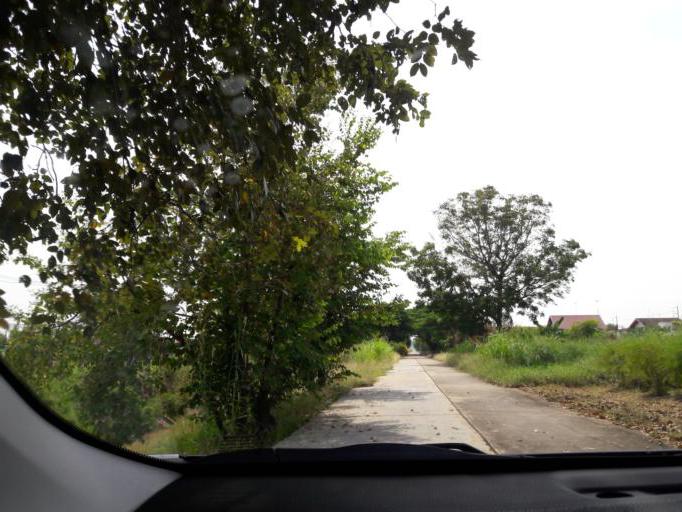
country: TH
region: Ang Thong
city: Ang Thong
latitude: 14.5761
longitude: 100.4545
